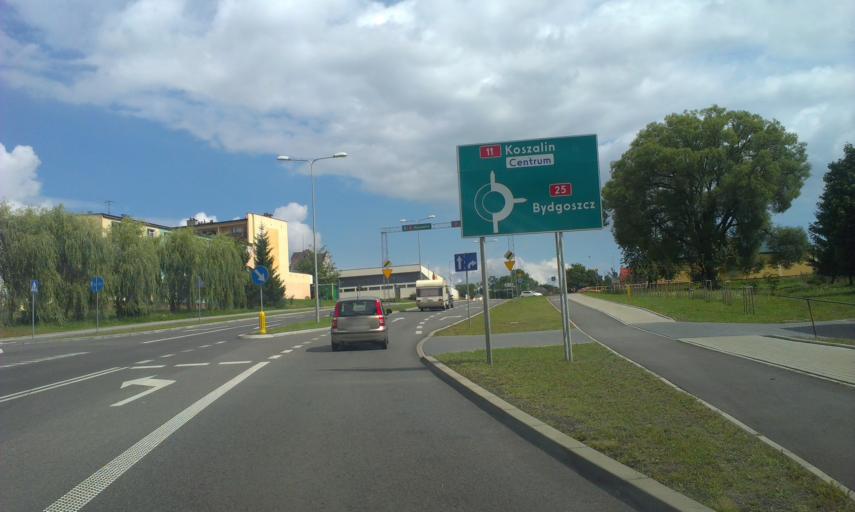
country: PL
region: West Pomeranian Voivodeship
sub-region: Powiat koszalinski
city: Bobolice
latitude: 53.9515
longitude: 16.5863
